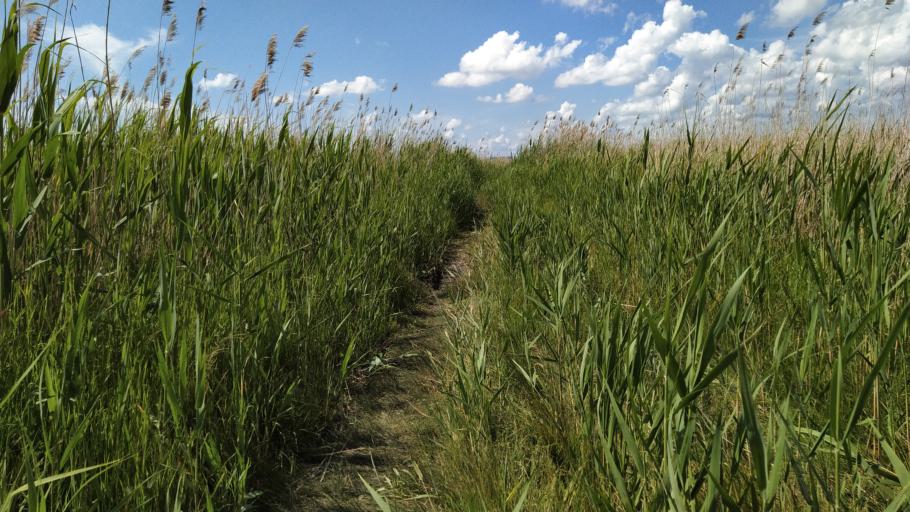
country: RU
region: Rostov
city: Bataysk
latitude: 47.1360
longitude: 39.6703
